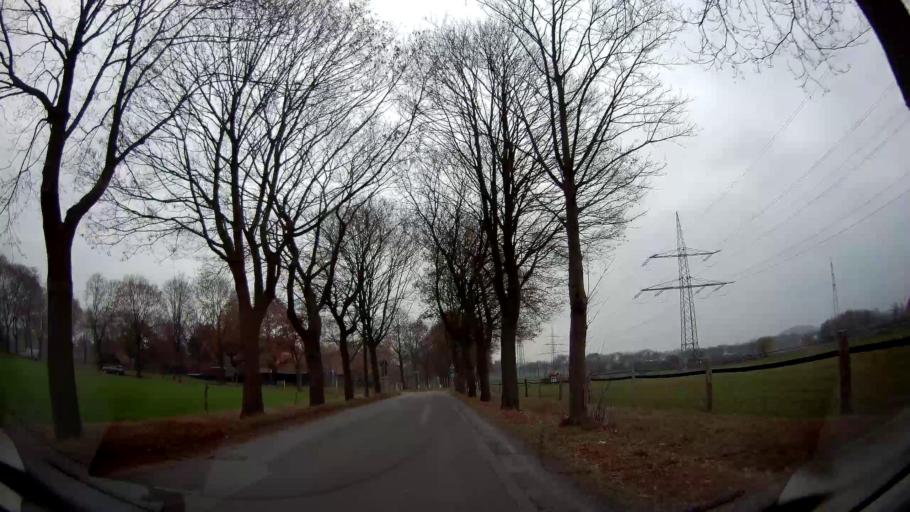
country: DE
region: North Rhine-Westphalia
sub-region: Regierungsbezirk Munster
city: Gladbeck
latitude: 51.5687
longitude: 7.0205
